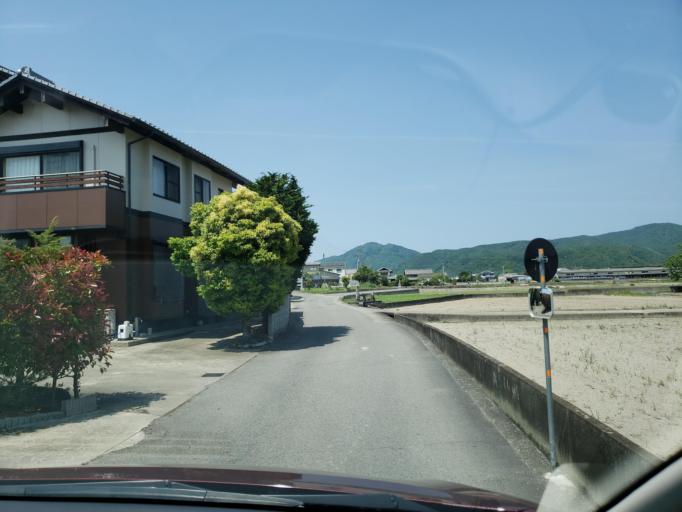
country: JP
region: Tokushima
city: Kamojimacho-jogejima
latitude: 34.0872
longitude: 134.2680
